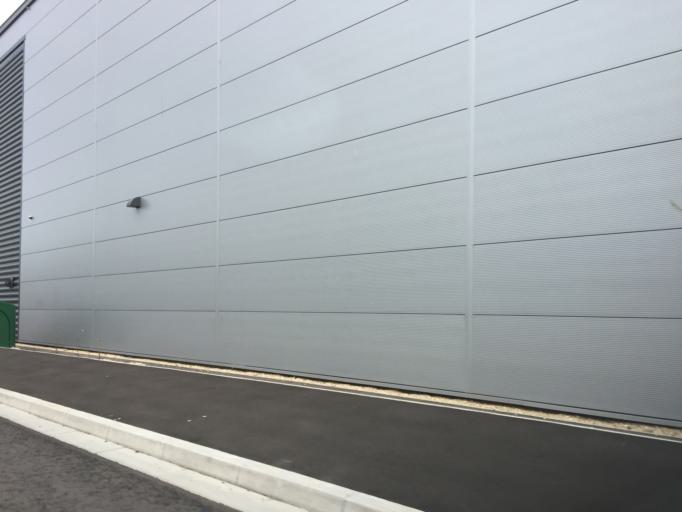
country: GB
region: England
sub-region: South Gloucestershire
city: Stoke Gifford
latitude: 51.5201
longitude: -2.5630
